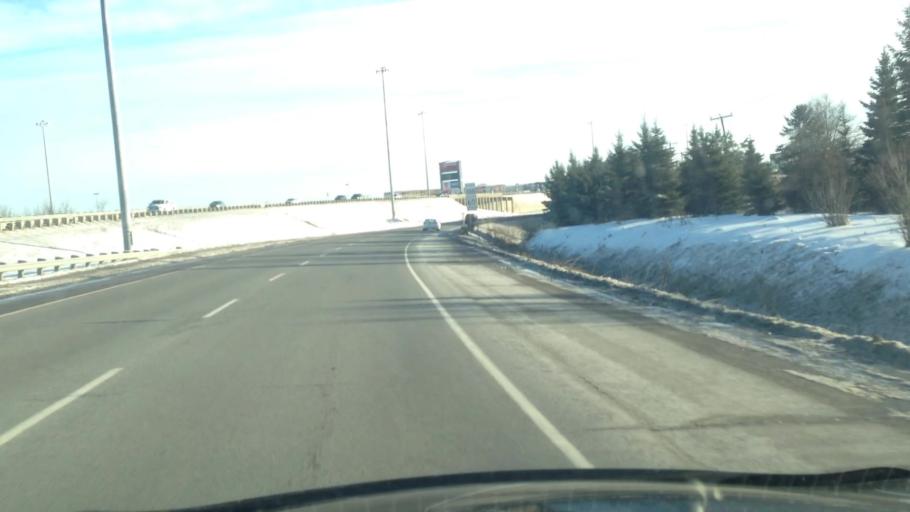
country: CA
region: Quebec
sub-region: Laurentides
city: Saint-Jerome
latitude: 45.7949
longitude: -74.0233
